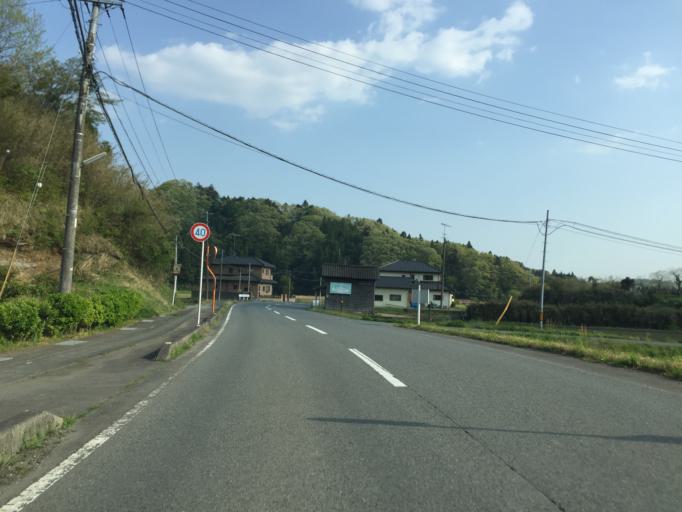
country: JP
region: Fukushima
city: Iwaki
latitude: 36.9830
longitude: 140.8006
